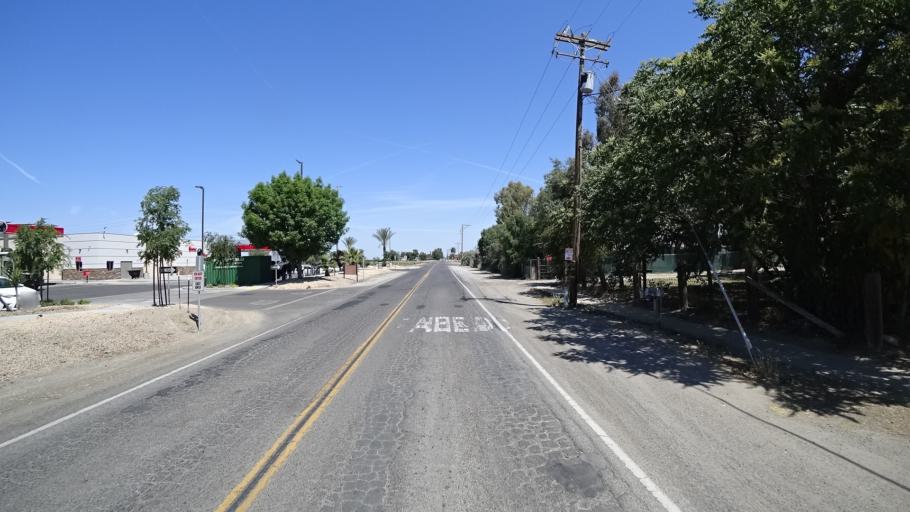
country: US
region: California
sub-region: Kings County
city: Lemoore
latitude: 36.2390
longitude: -119.7628
